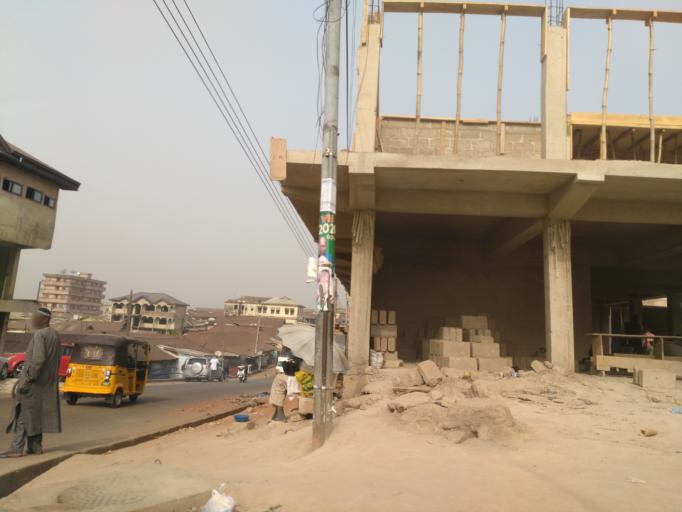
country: GH
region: Ashanti
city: Kumasi
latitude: 6.6998
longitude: -1.6136
